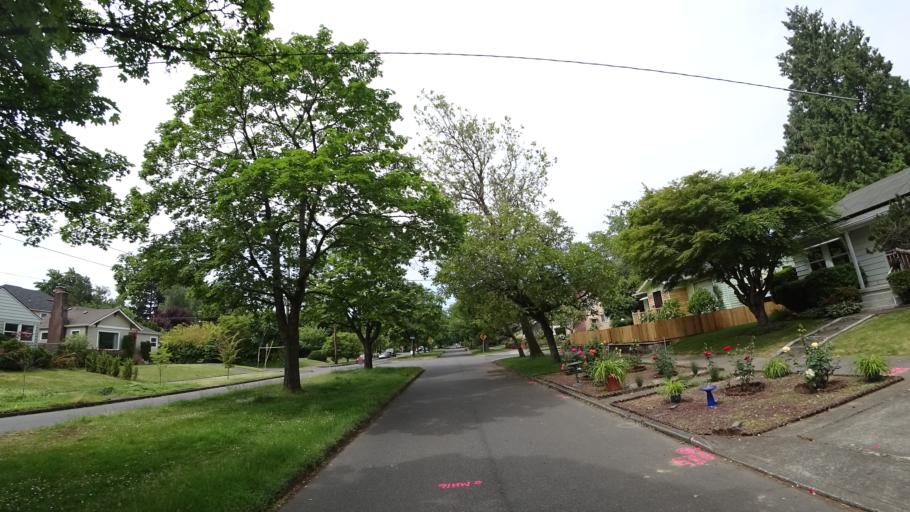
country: US
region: Oregon
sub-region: Multnomah County
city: Portland
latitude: 45.5664
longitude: -122.6290
